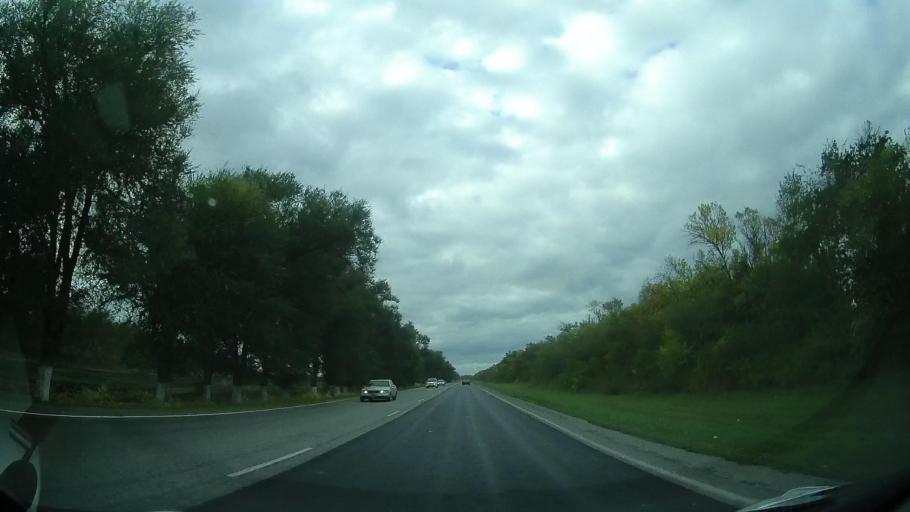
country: RU
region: Rostov
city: Zernograd
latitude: 46.7977
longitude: 40.3713
